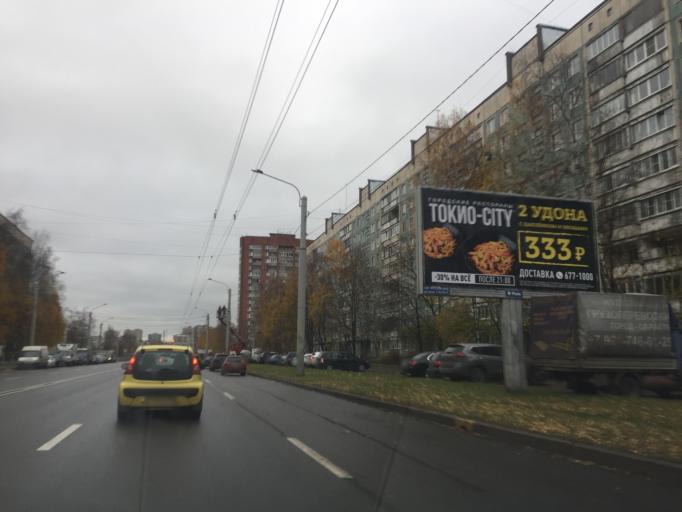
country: RU
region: Leningrad
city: Akademicheskoe
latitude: 60.0239
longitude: 30.3801
